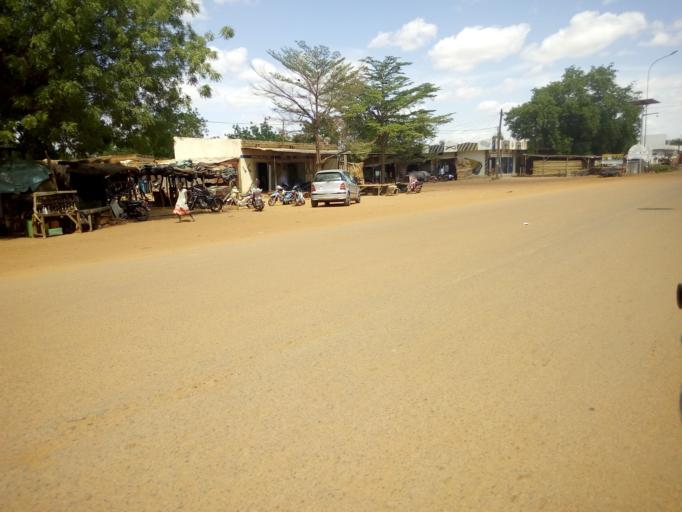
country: ML
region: Segou
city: Segou
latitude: 13.4352
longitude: -6.2644
